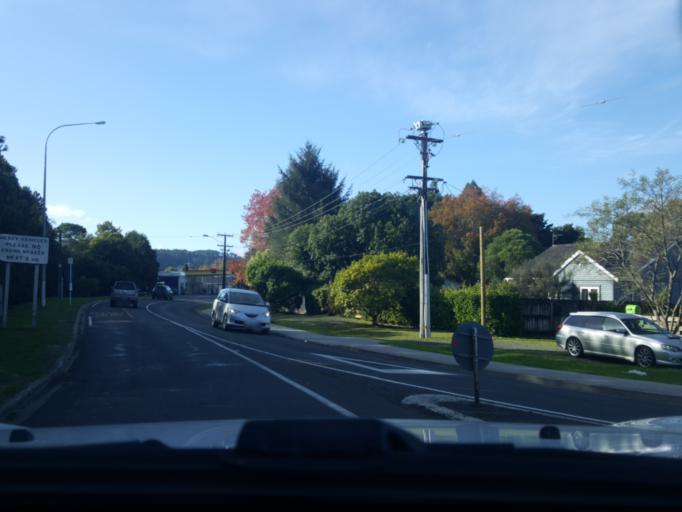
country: NZ
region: Auckland
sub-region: Auckland
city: Rosebank
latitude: -36.7625
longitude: 174.5875
